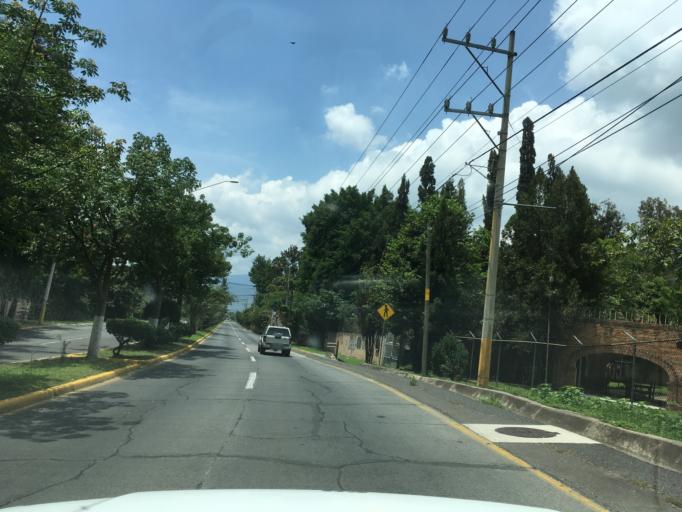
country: MX
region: Jalisco
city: Tlajomulco de Zuniga
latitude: 20.4848
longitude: -103.4570
